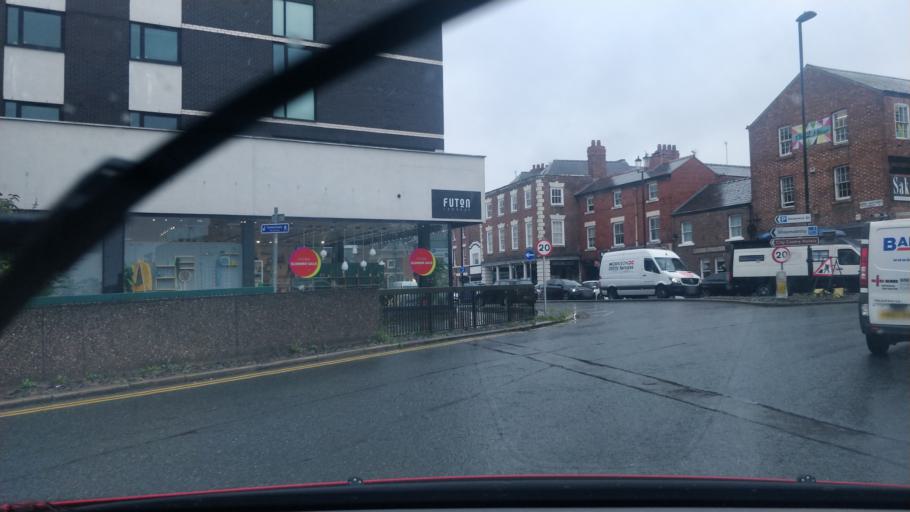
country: GB
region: England
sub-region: Cheshire West and Chester
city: Chester
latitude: 53.1953
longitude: -2.8935
